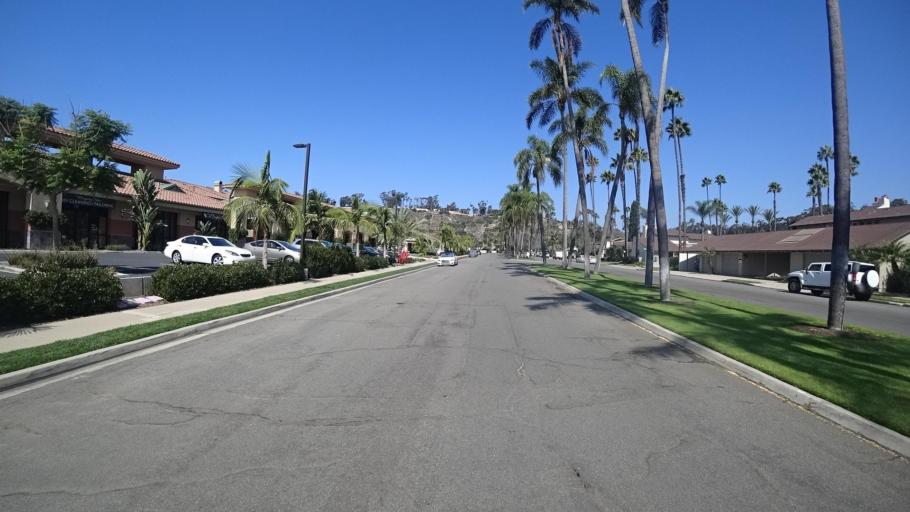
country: US
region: California
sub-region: San Diego County
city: Fairbanks Ranch
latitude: 32.9918
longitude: -117.2122
